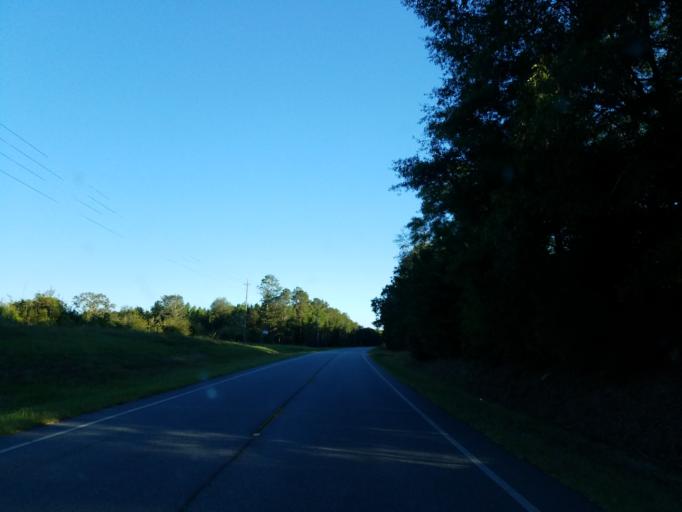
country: US
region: Georgia
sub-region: Worth County
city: Sylvester
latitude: 31.6628
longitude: -83.8705
